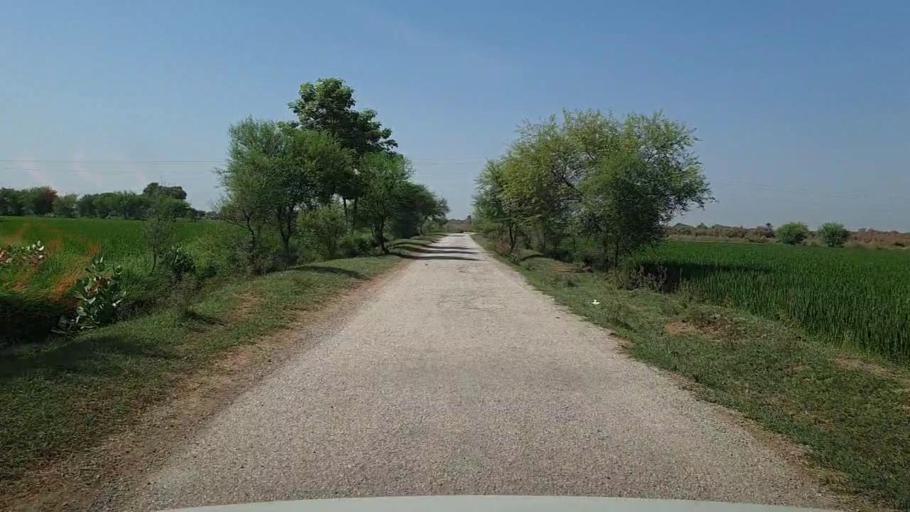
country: PK
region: Sindh
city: Kandhkot
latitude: 28.3335
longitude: 69.3665
